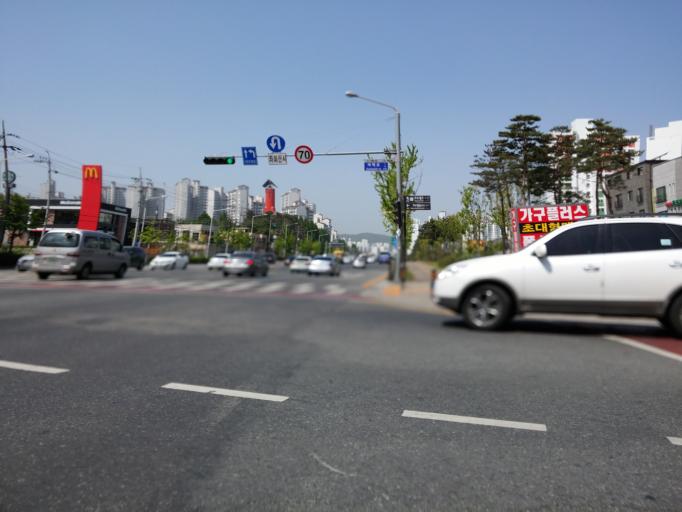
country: KR
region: Daejeon
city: Daejeon
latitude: 36.3044
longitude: 127.3494
